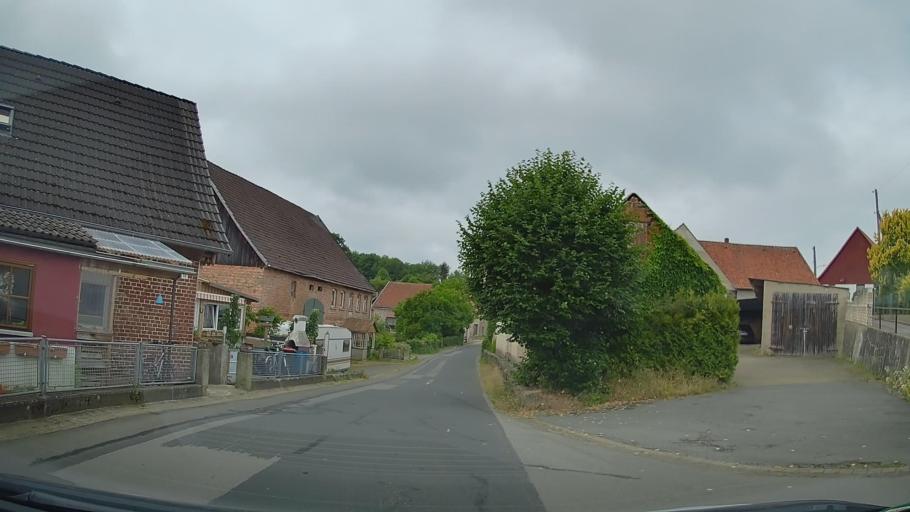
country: DE
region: Lower Saxony
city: Aerzen
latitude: 52.0518
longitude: 9.1757
